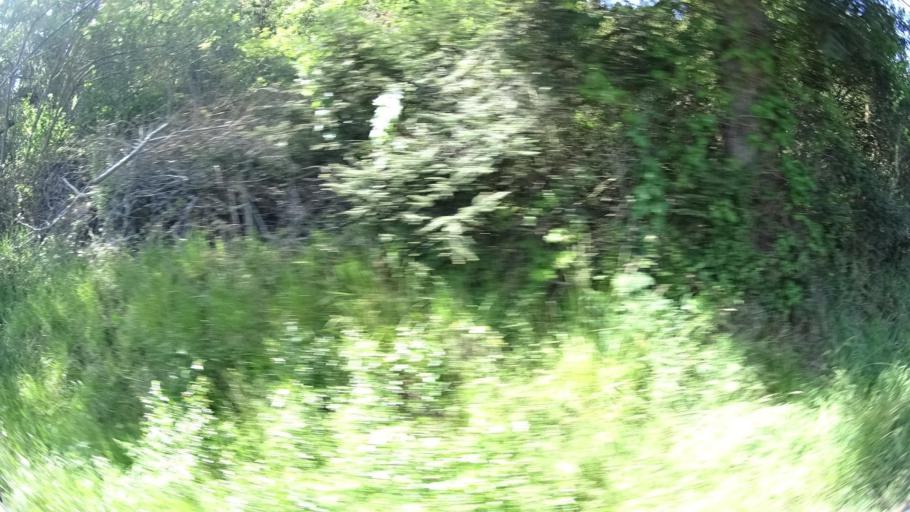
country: US
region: California
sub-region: Humboldt County
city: Hydesville
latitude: 40.5565
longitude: -124.1072
